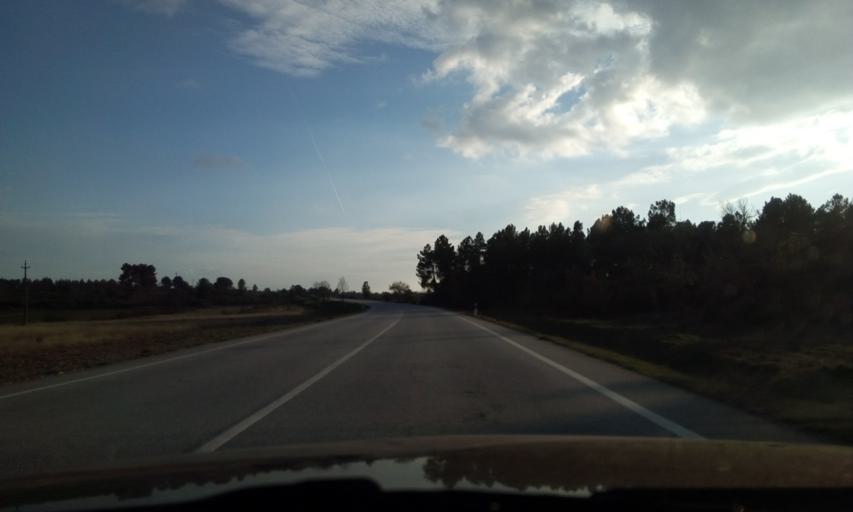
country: PT
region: Guarda
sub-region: Pinhel
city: Pinhel
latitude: 40.6380
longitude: -6.9719
